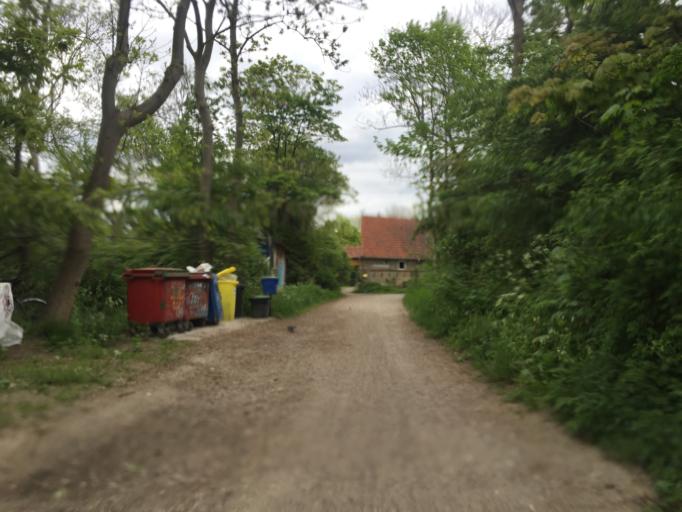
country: DK
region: Capital Region
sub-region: Kobenhavn
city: Christianshavn
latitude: 55.6738
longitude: 12.6081
